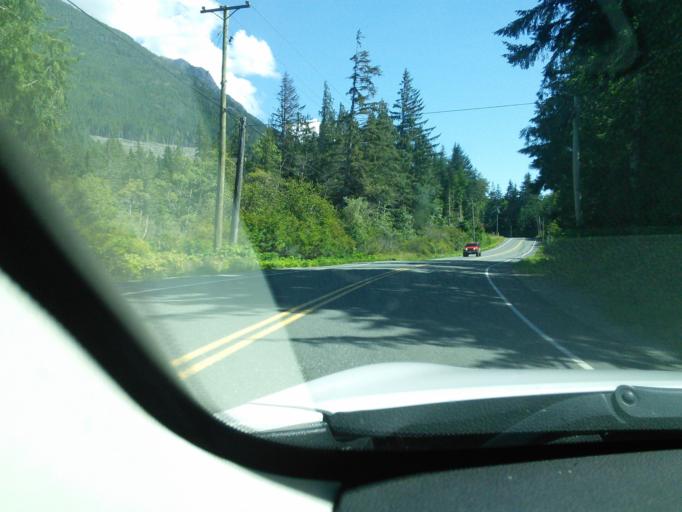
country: CA
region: British Columbia
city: Campbell River
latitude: 50.3536
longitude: -125.9088
